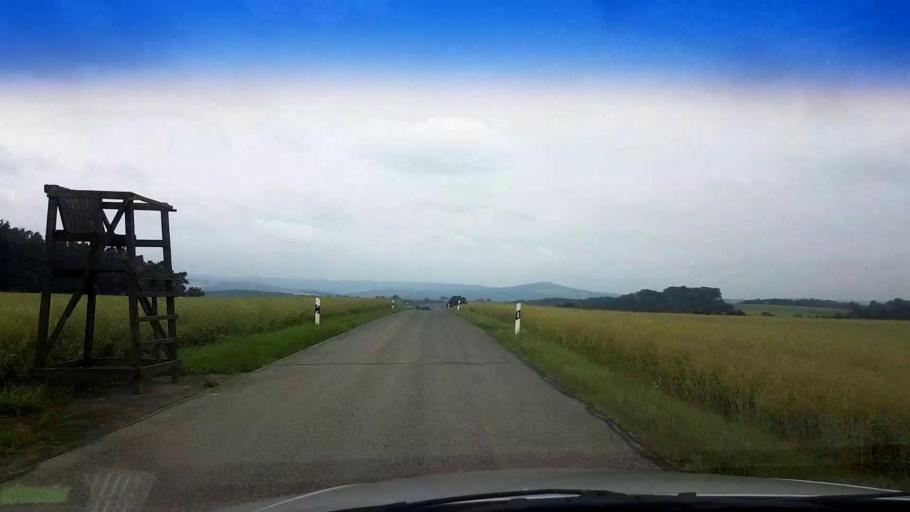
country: DE
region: Bavaria
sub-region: Upper Franconia
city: Kasendorf
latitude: 50.0754
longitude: 11.3374
